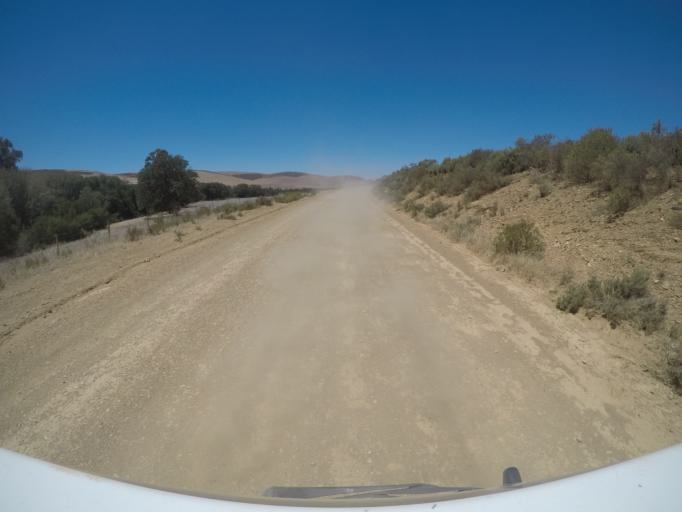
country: ZA
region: Western Cape
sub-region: Overberg District Municipality
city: Grabouw
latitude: -34.0964
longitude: 19.1984
